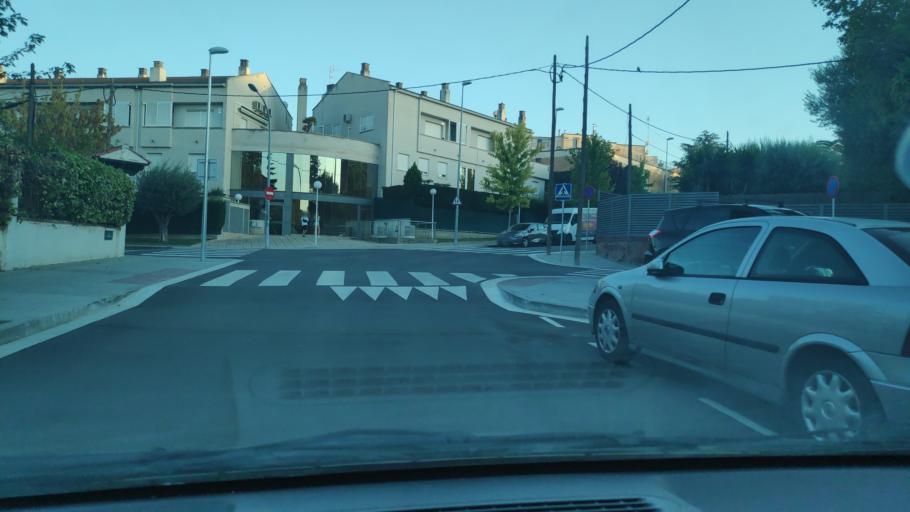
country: ES
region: Catalonia
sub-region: Provincia de Barcelona
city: Cerdanyola del Valles
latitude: 41.4874
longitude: 2.1423
